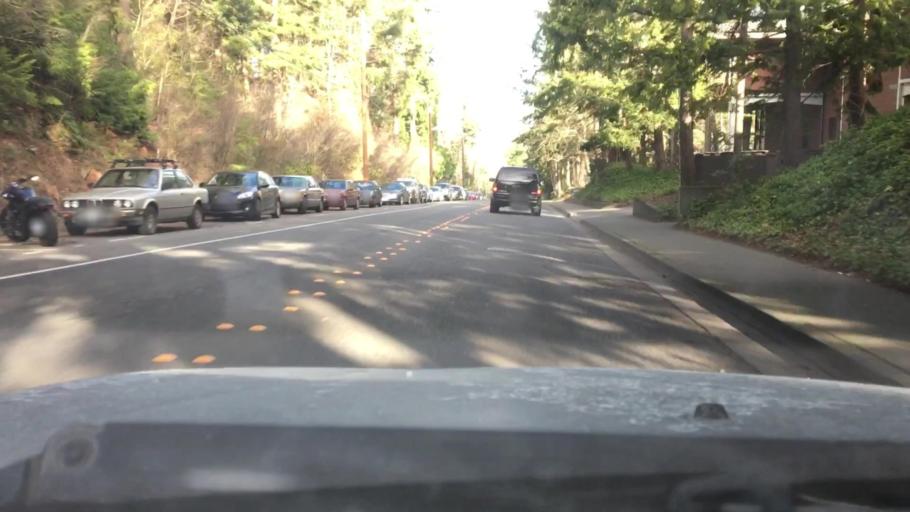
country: US
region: Washington
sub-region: Whatcom County
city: Bellingham
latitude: 48.7345
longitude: -122.4902
